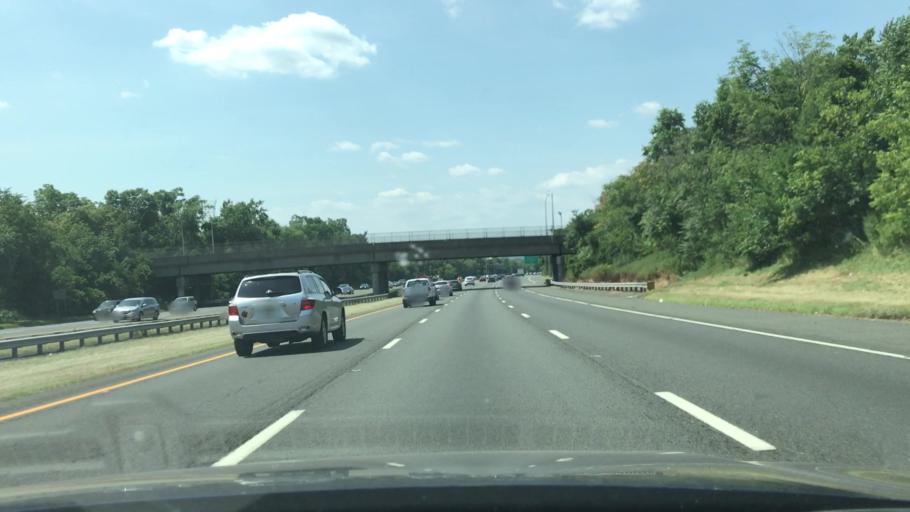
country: US
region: New Jersey
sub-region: Somerset County
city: South Bound Brook
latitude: 40.5467
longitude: -74.5369
